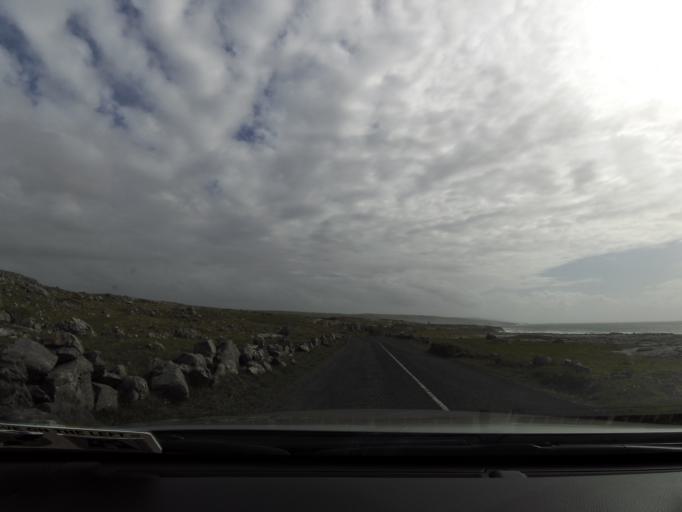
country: IE
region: Connaught
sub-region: County Galway
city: Bearna
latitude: 53.0667
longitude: -9.3592
